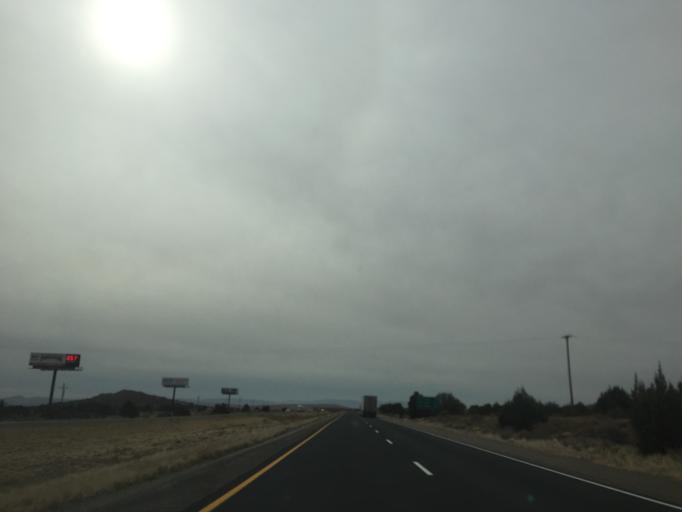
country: US
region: Utah
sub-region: Washington County
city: Toquerville
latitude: 37.2745
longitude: -113.3157
